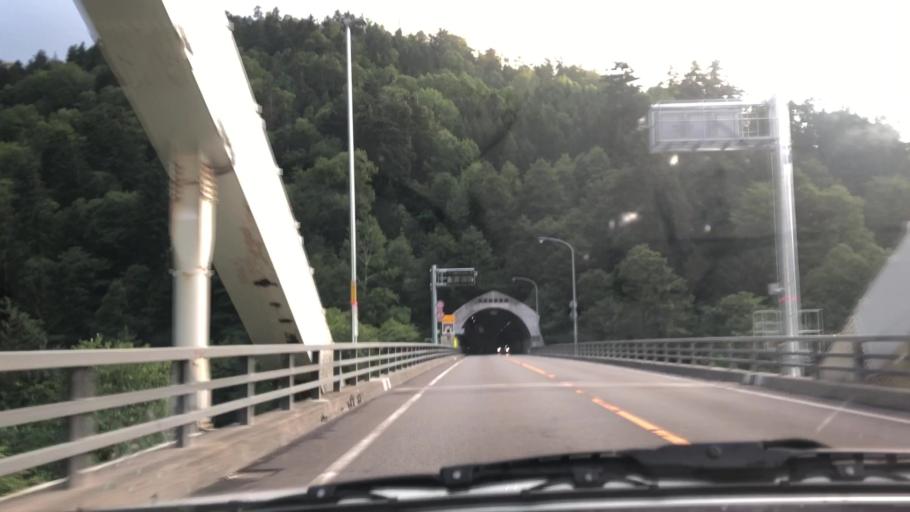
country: JP
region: Hokkaido
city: Shimo-furano
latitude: 42.9038
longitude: 142.3228
